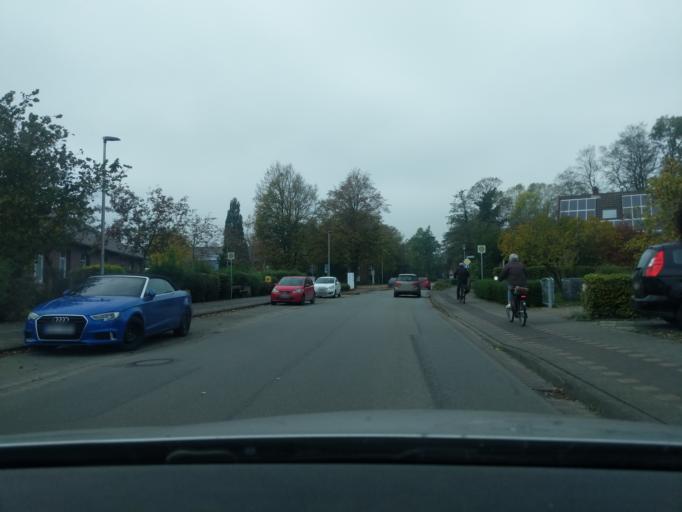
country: DE
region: Lower Saxony
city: Otterndorf
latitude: 53.8128
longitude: 8.8895
